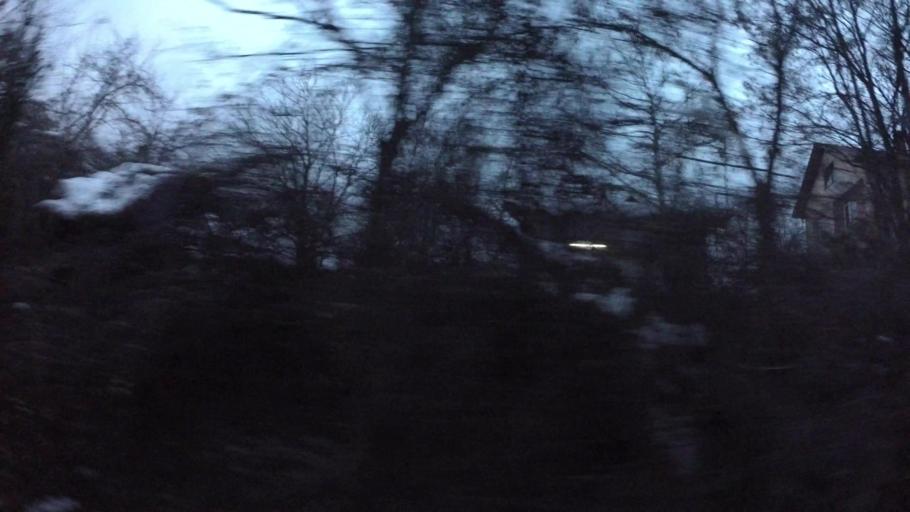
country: BA
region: Federation of Bosnia and Herzegovina
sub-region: Kanton Sarajevo
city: Sarajevo
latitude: 43.8533
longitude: 18.3403
